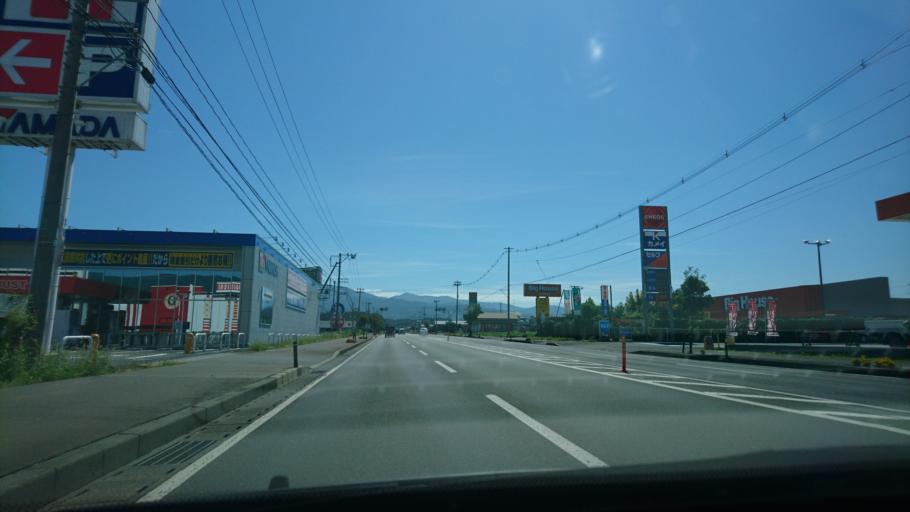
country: JP
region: Iwate
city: Tono
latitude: 39.3351
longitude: 141.5501
